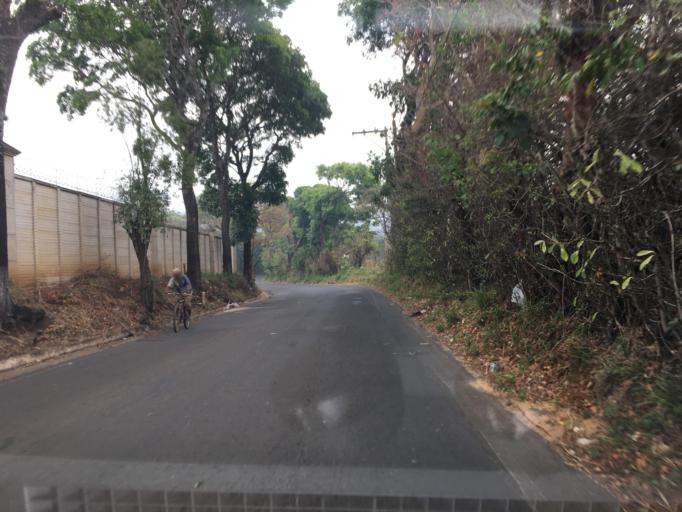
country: GT
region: Guatemala
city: Fraijanes
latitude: 14.3856
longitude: -90.4891
